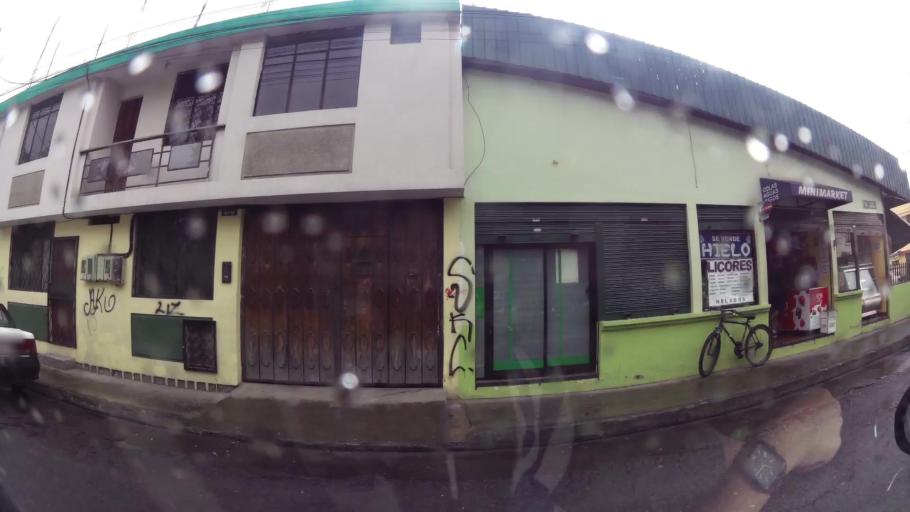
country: EC
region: Pichincha
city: Sangolqui
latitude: -0.2987
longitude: -78.4807
